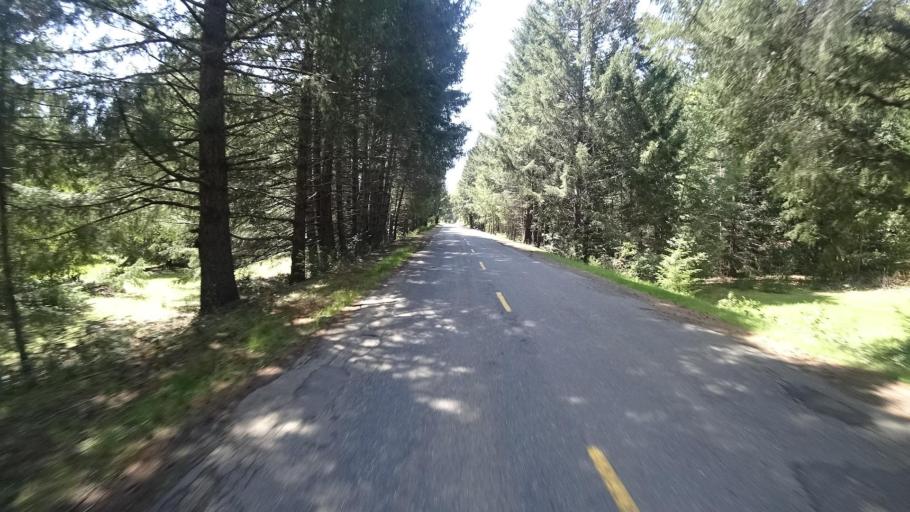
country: US
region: California
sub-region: Humboldt County
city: Redway
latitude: 40.1192
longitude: -123.6711
